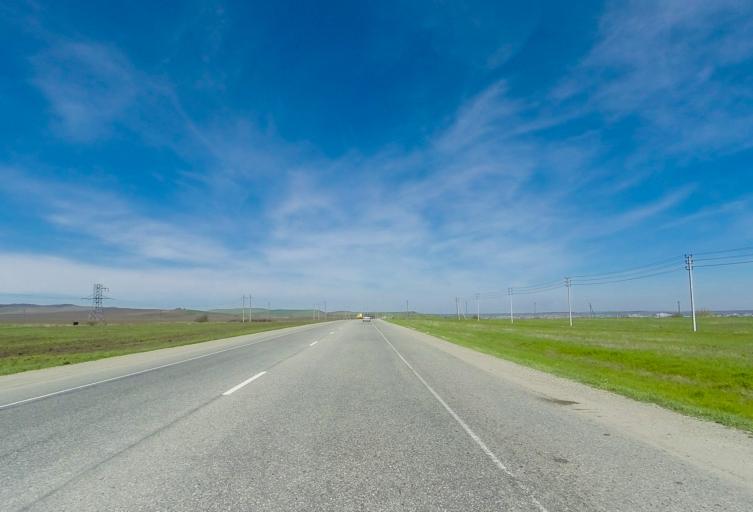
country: RU
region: Kabardino-Balkariya
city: Dugulubgey
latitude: 43.6515
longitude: 43.5136
